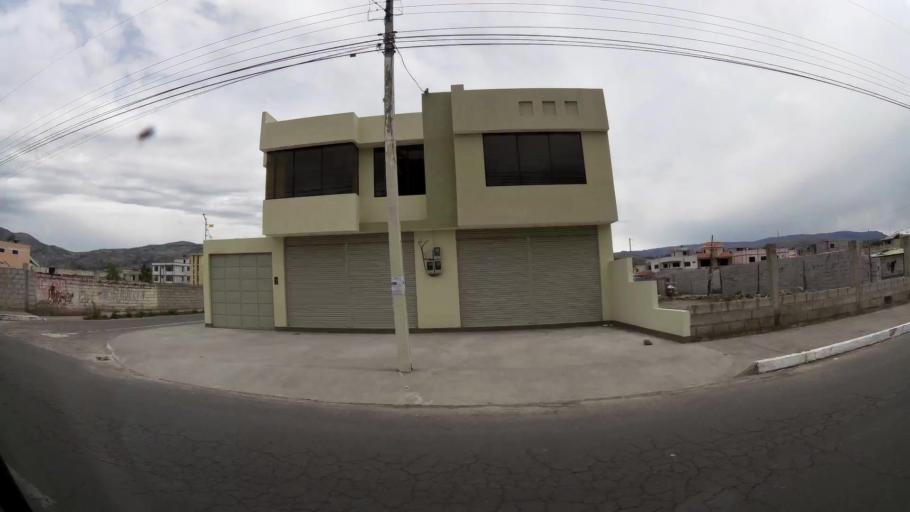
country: EC
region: Cotopaxi
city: San Miguel de Salcedo
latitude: -1.0348
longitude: -78.5907
